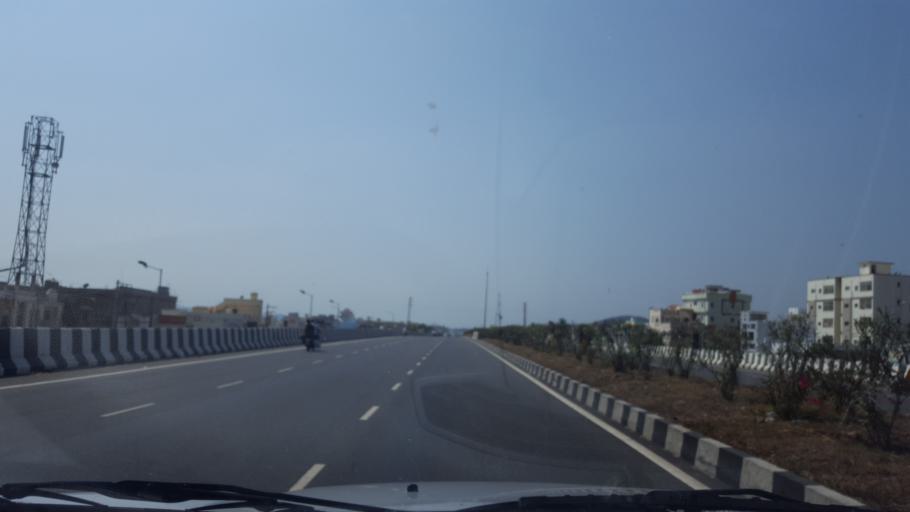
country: IN
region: Andhra Pradesh
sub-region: Guntur
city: Chilakalurupet
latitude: 15.9856
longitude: 80.1036
